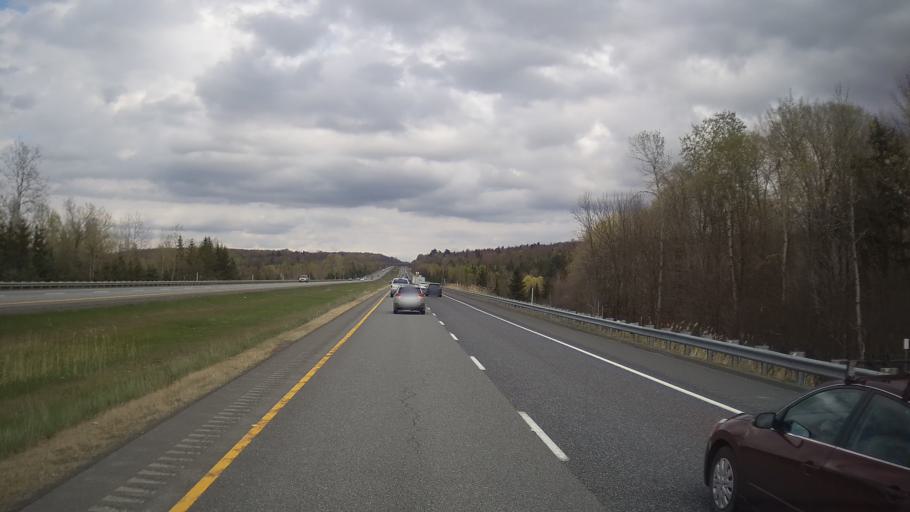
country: CA
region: Quebec
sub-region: Monteregie
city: Waterloo
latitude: 45.3015
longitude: -72.4397
